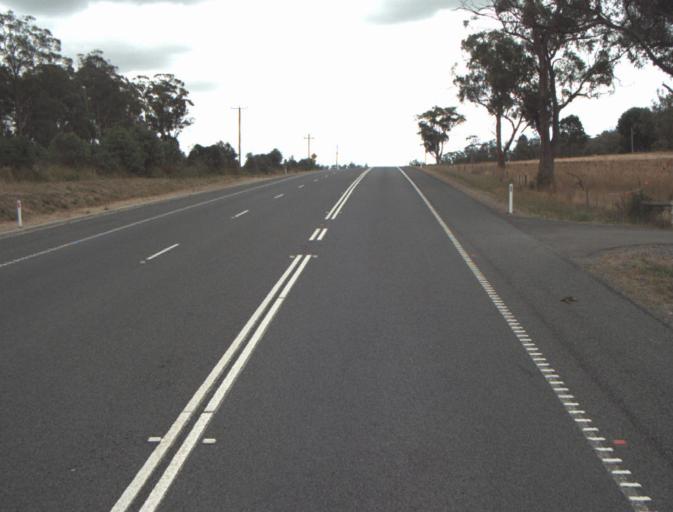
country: AU
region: Tasmania
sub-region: Launceston
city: Mayfield
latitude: -41.2586
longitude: 147.0261
